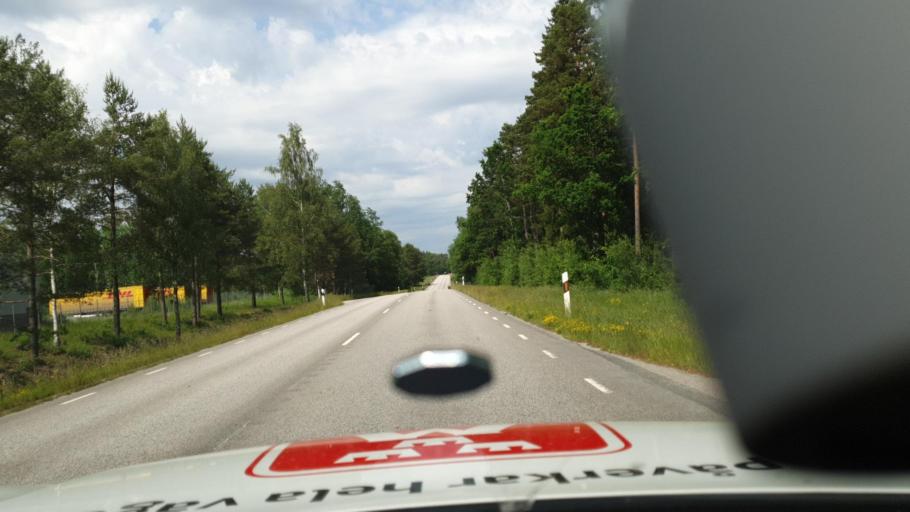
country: SE
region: Joenkoeping
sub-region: Varnamo Kommun
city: Varnamo
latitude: 57.2155
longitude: 14.0403
